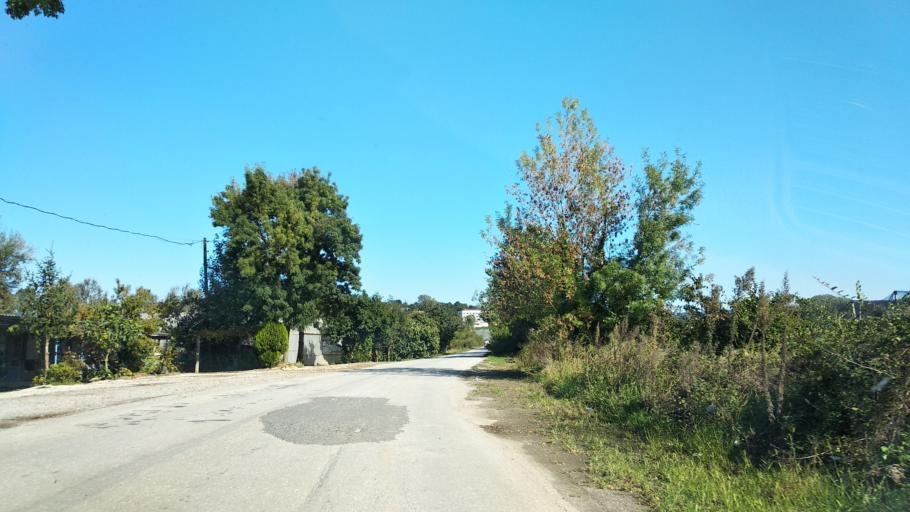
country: TR
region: Sakarya
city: Ortakoy
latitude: 41.0329
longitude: 30.6116
